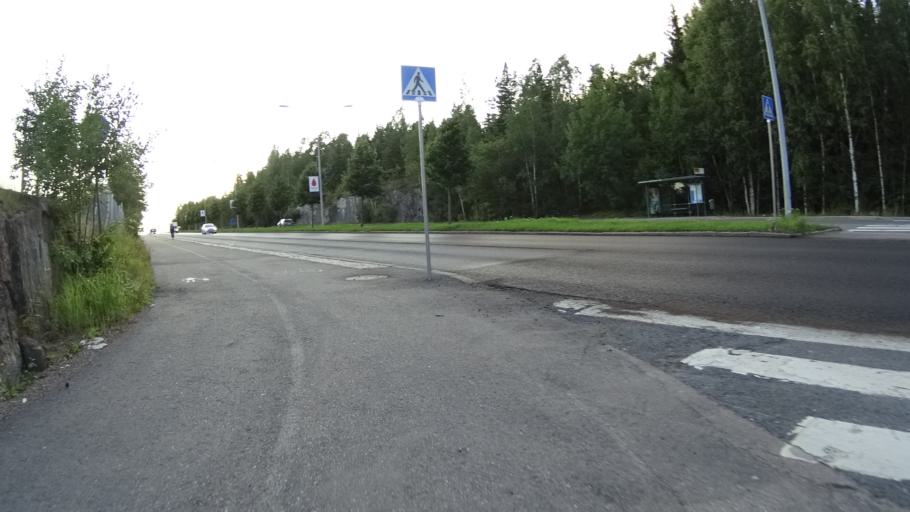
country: FI
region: Uusimaa
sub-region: Helsinki
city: Helsinki
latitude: 60.2207
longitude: 24.9286
